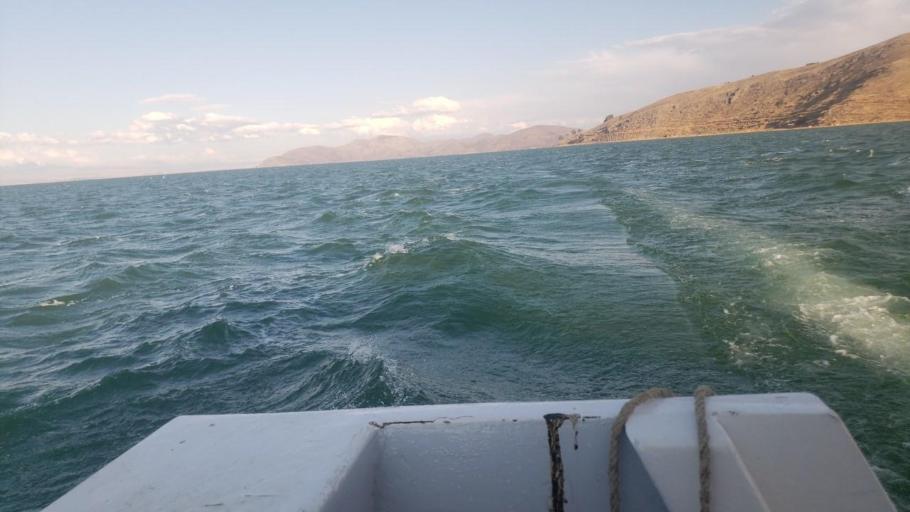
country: BO
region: La Paz
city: San Pablo
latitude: -16.2906
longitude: -68.7630
